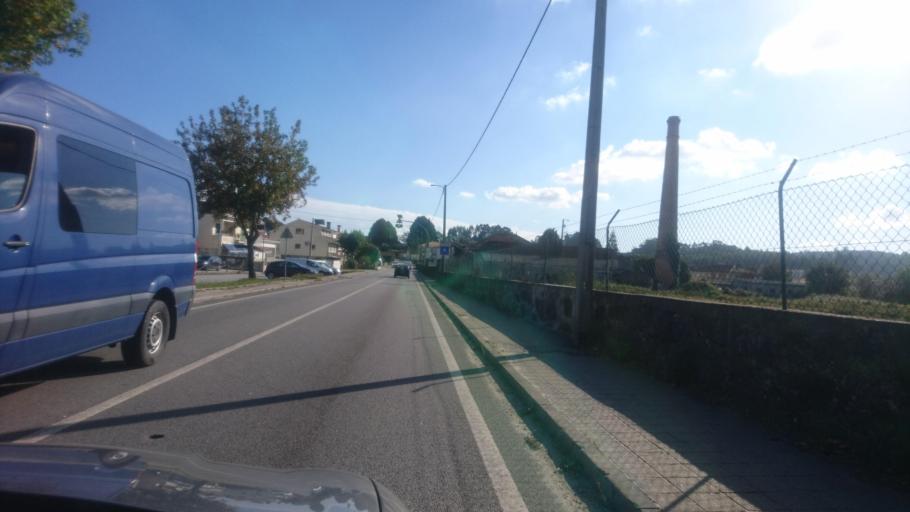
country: PT
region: Porto
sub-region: Paredes
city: Madalena
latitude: 41.2330
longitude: -8.3635
